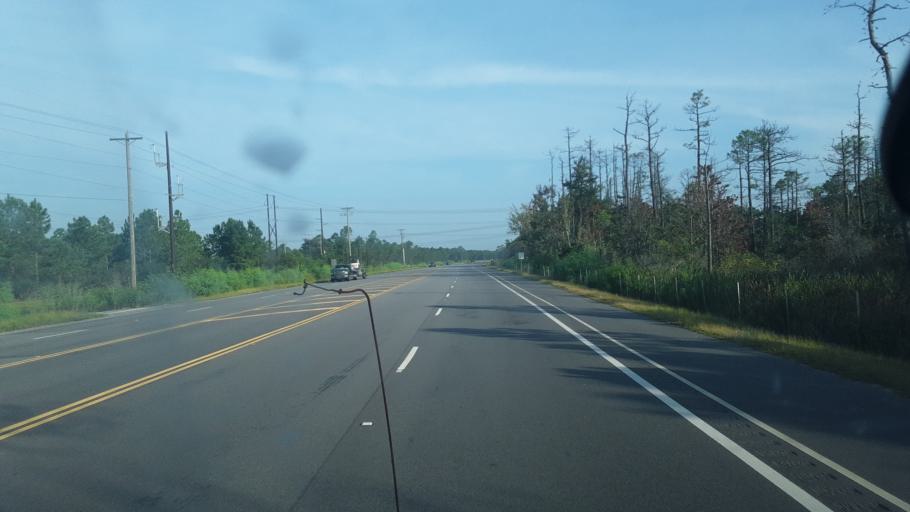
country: US
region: South Carolina
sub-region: Horry County
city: Myrtle Beach
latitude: 33.7844
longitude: -78.8768
